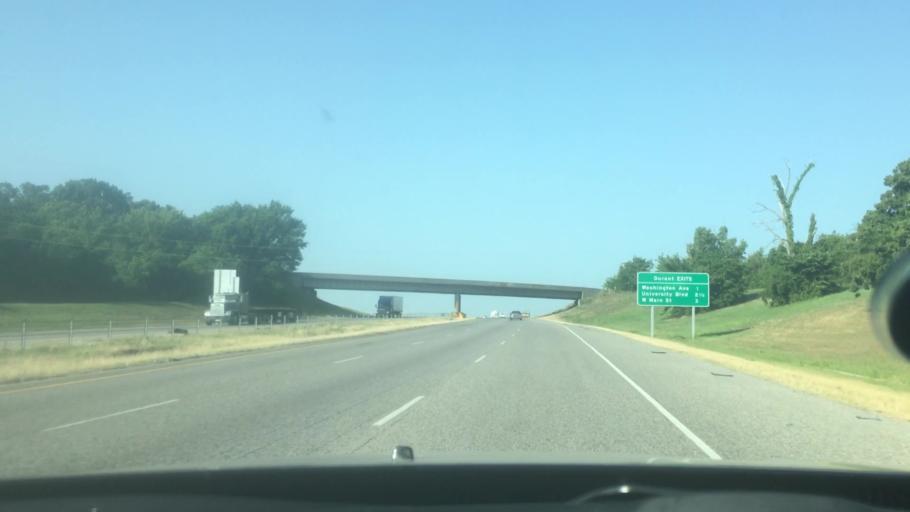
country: US
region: Oklahoma
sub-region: Bryan County
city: Durant
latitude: 34.0353
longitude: -96.3786
